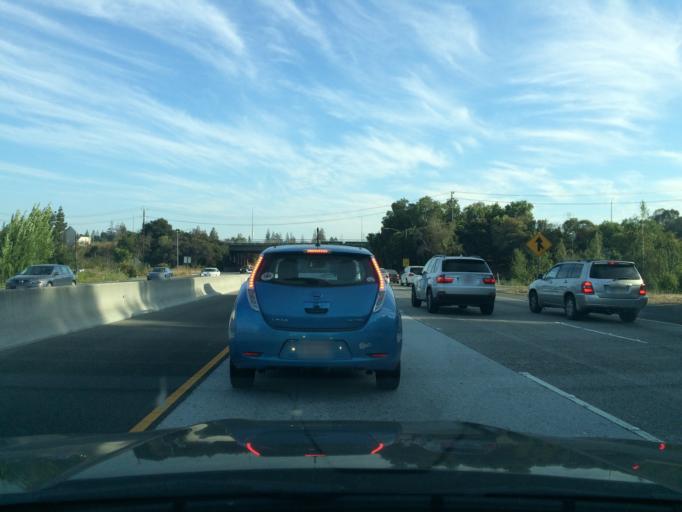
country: US
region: California
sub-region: Santa Clara County
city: Mountain View
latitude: 37.3798
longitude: -122.0679
